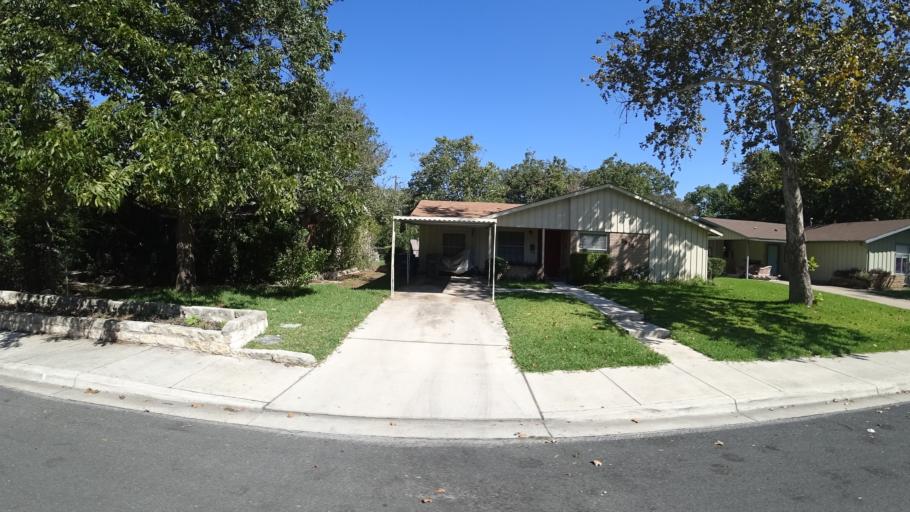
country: US
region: Texas
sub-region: Travis County
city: Austin
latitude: 30.3098
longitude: -97.7029
